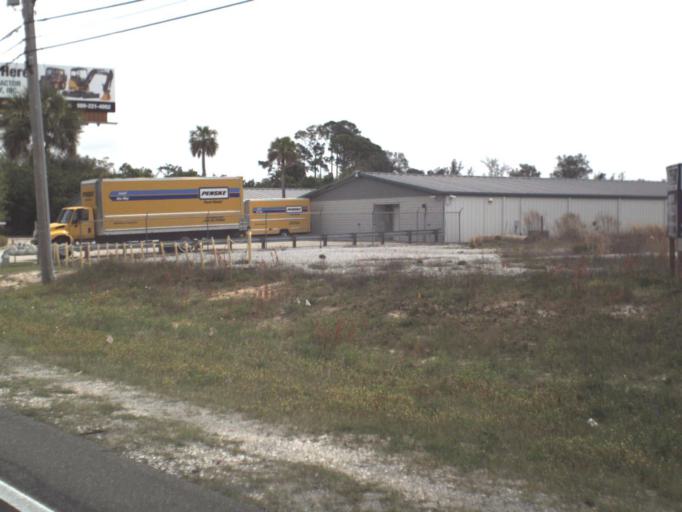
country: US
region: Florida
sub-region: Santa Rosa County
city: Tiger Point
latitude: 30.3959
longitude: -87.0254
